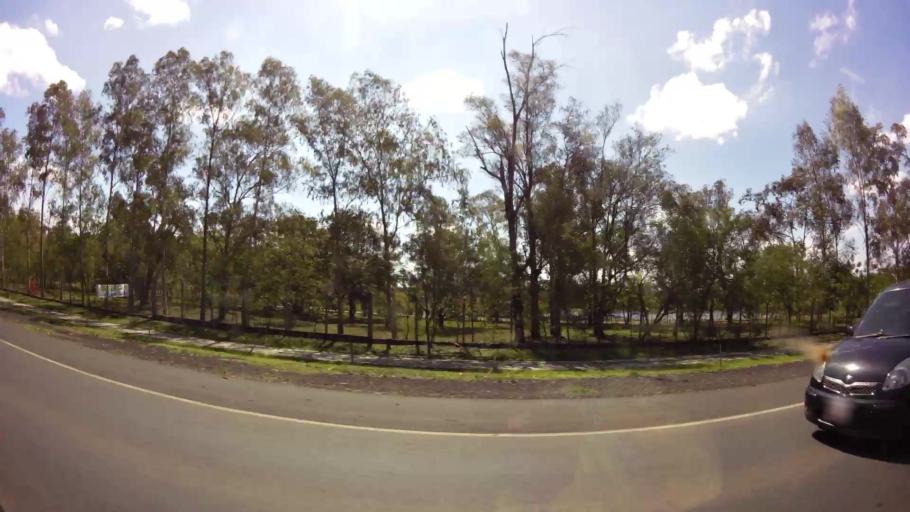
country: PY
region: Central
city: Fernando de la Mora
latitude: -25.2663
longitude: -57.5357
